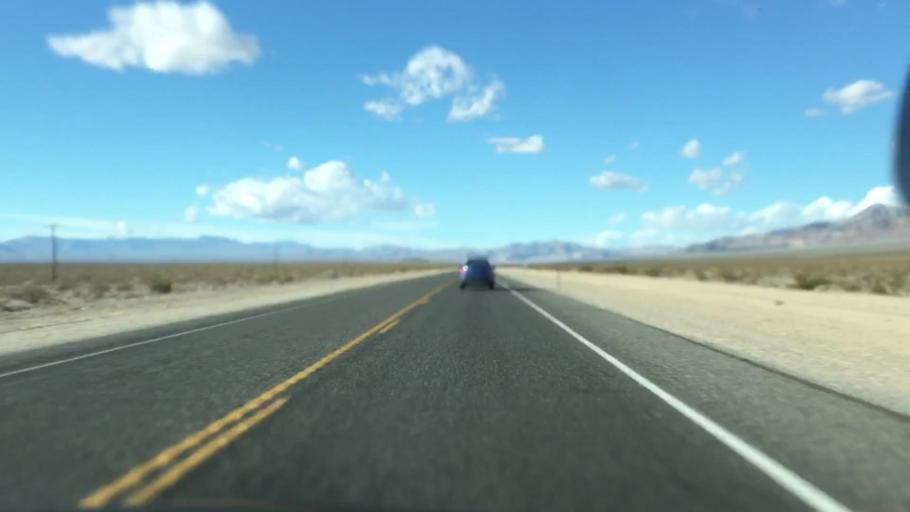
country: US
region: Nevada
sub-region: Nye County
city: Beatty
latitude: 36.7430
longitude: -116.6474
